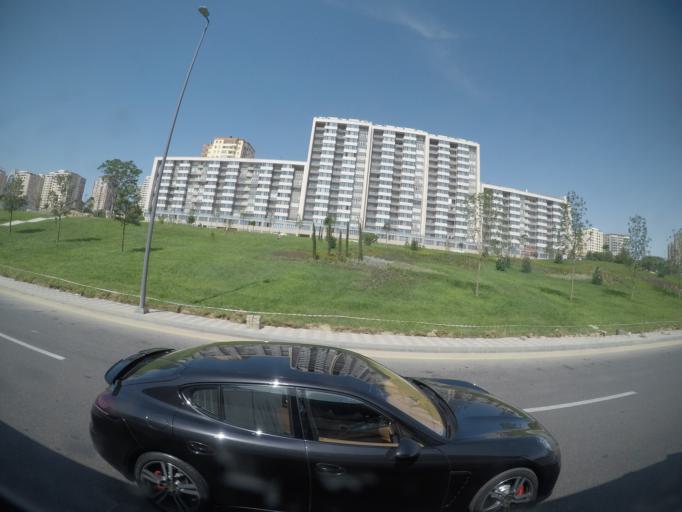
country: AZ
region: Baki
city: Badamdar
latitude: 40.3754
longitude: 49.8253
